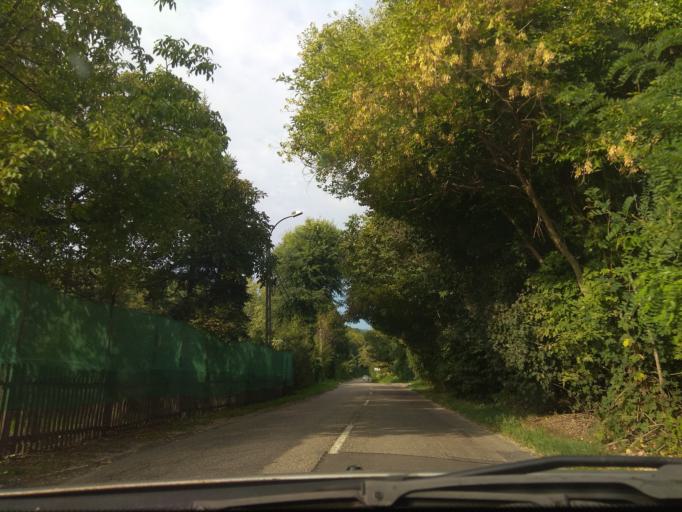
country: HU
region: Borsod-Abauj-Zemplen
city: Miskolc
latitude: 48.0861
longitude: 20.7122
